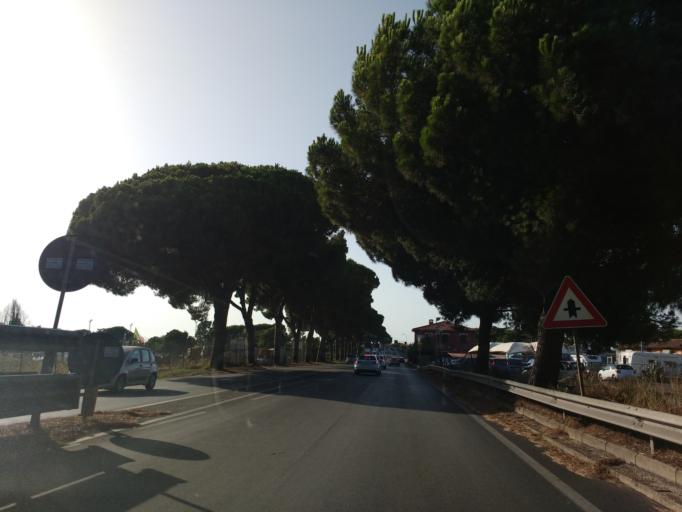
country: IT
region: Latium
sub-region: Citta metropolitana di Roma Capitale
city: Marino
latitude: 41.7741
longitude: 12.6097
